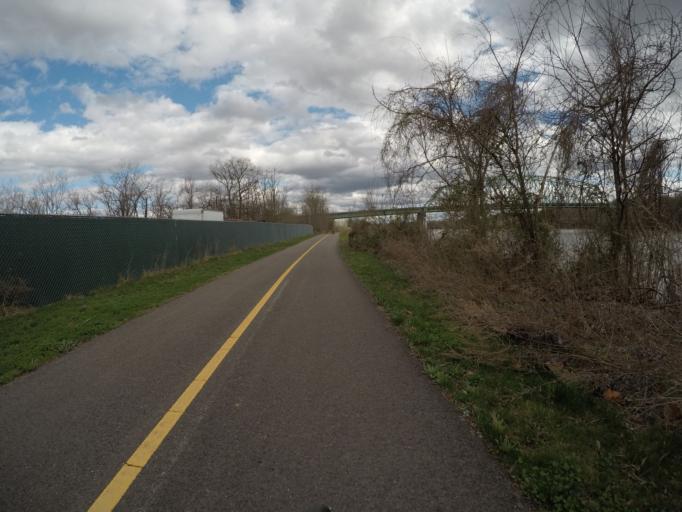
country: US
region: West Virginia
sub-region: Wood County
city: Williamstown
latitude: 39.4071
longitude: -81.4309
